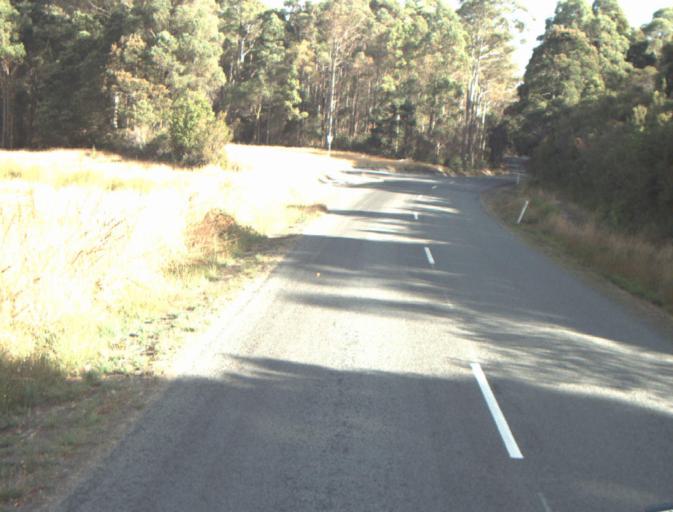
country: AU
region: Tasmania
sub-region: Dorset
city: Bridport
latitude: -41.1606
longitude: 147.2394
